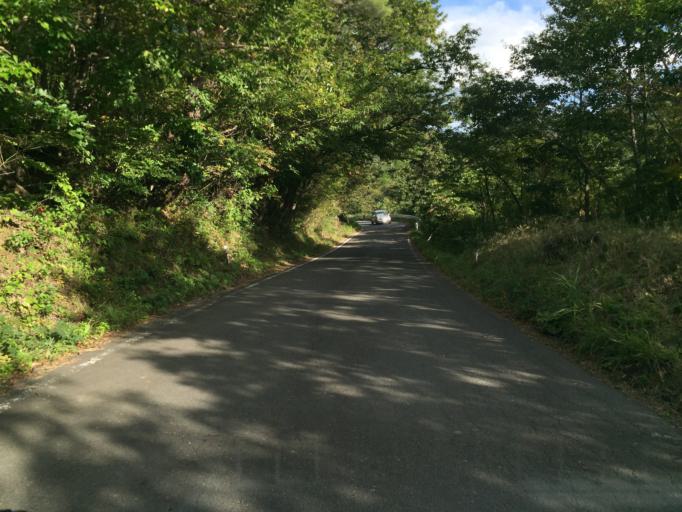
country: JP
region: Fukushima
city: Nihommatsu
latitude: 37.6758
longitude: 140.3665
